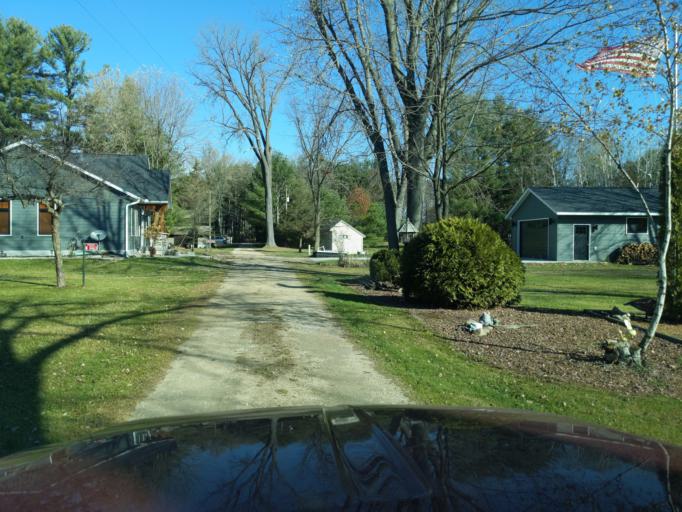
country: US
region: Wisconsin
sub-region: Waushara County
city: Wautoma
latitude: 44.0317
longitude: -89.3015
